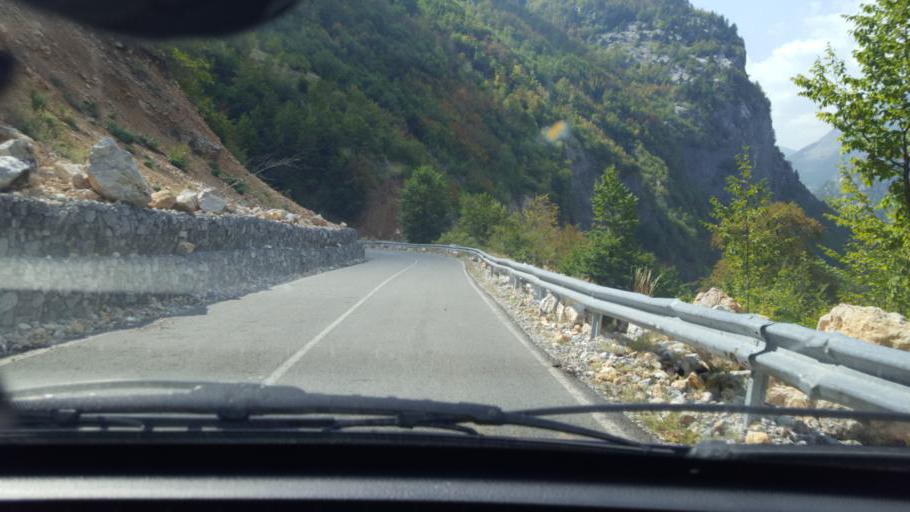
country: ME
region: Andrijevica
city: Andrijevica
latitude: 42.5340
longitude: 19.6736
